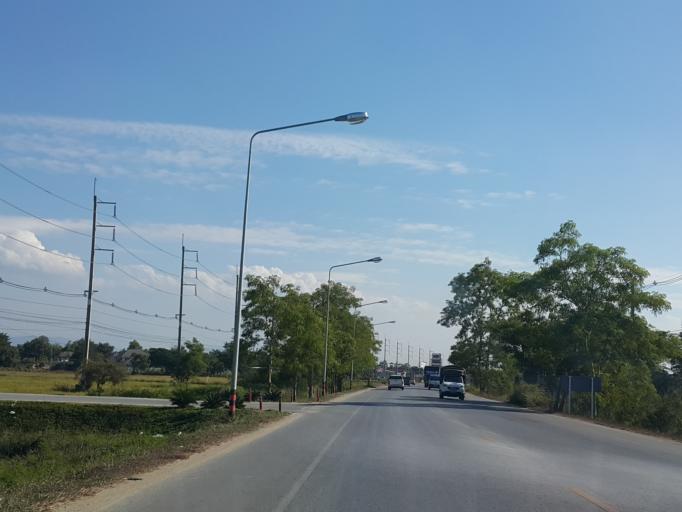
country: TH
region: Chiang Mai
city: San Sai
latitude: 18.7919
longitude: 99.0680
